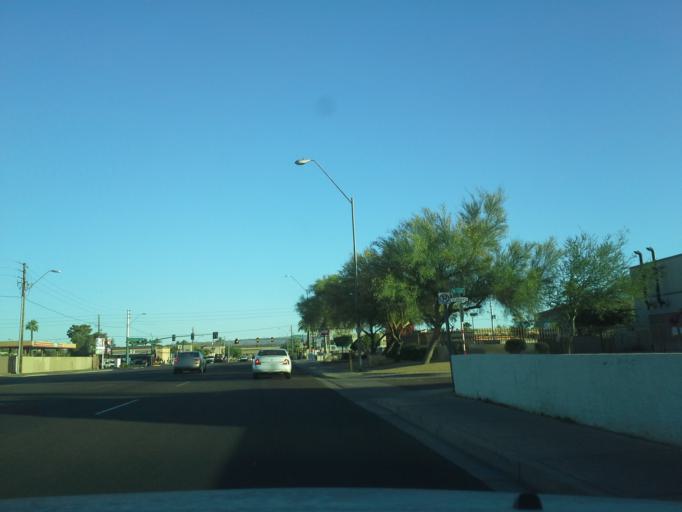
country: US
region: Arizona
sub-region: Maricopa County
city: Phoenix
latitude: 33.4673
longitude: -112.0304
